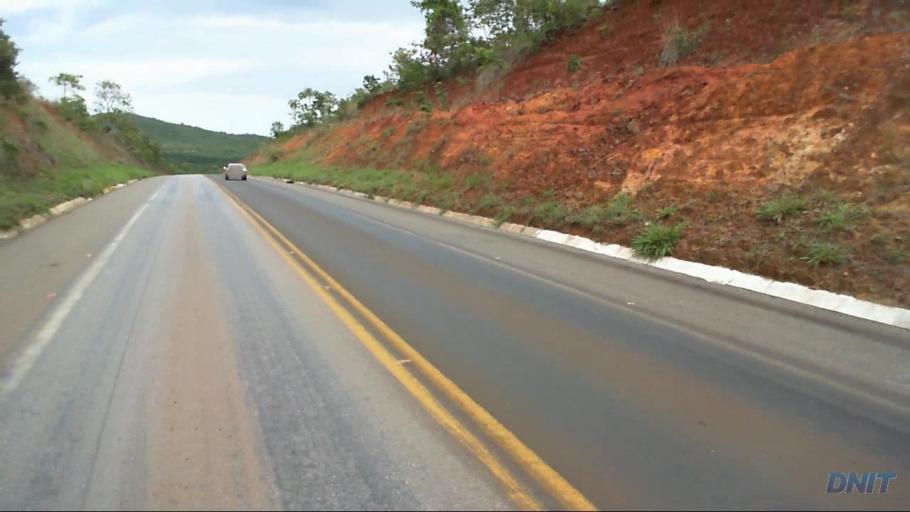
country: BR
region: Goias
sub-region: Barro Alto
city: Barro Alto
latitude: -14.9378
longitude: -48.9432
